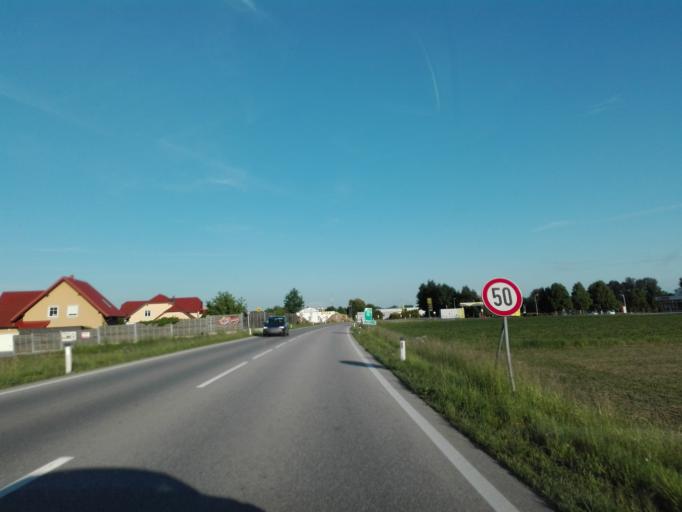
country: AT
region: Upper Austria
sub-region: Politischer Bezirk Urfahr-Umgebung
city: Feldkirchen an der Donau
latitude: 48.3613
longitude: 13.9934
